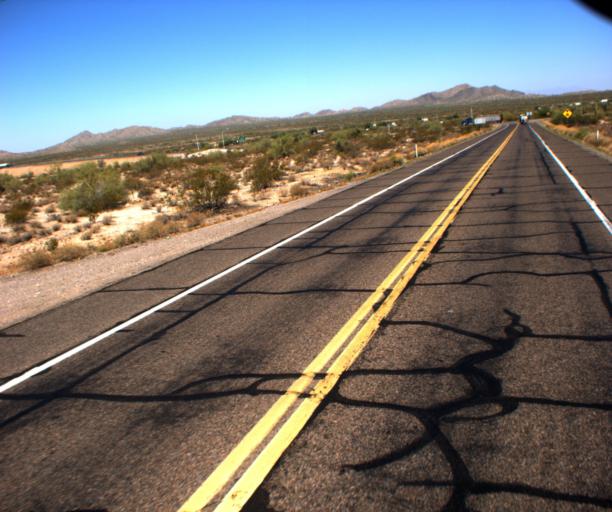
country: US
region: Arizona
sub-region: Pinal County
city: Sacaton
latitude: 33.0048
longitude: -111.7484
